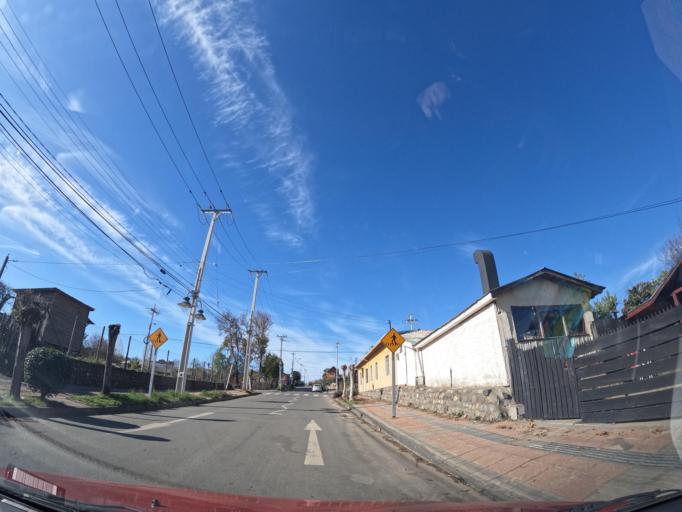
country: CL
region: Biobio
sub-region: Provincia de Biobio
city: Yumbel
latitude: -36.8249
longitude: -72.6652
